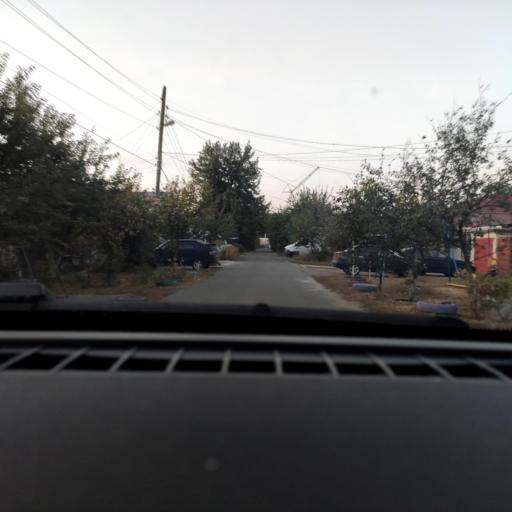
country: RU
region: Voronezj
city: Voronezh
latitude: 51.6648
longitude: 39.2580
